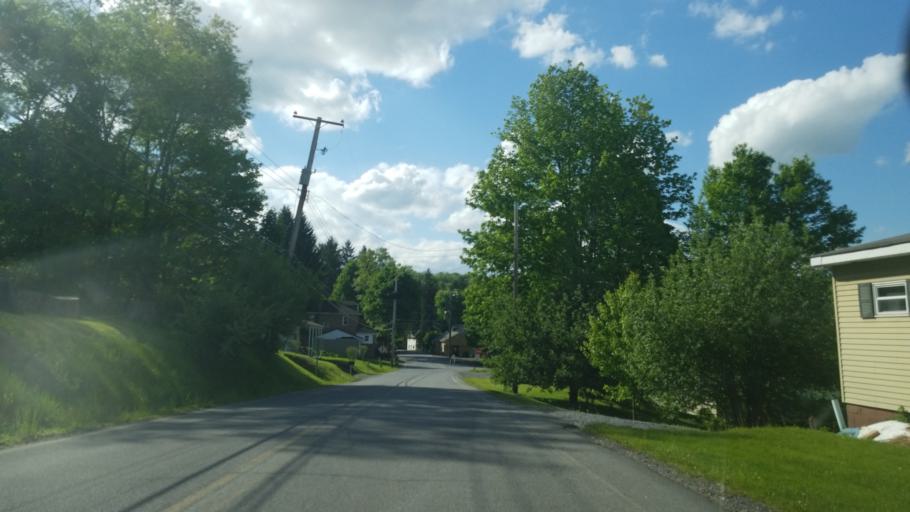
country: US
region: Pennsylvania
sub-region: Clearfield County
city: Troy
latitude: 40.9267
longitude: -78.2790
